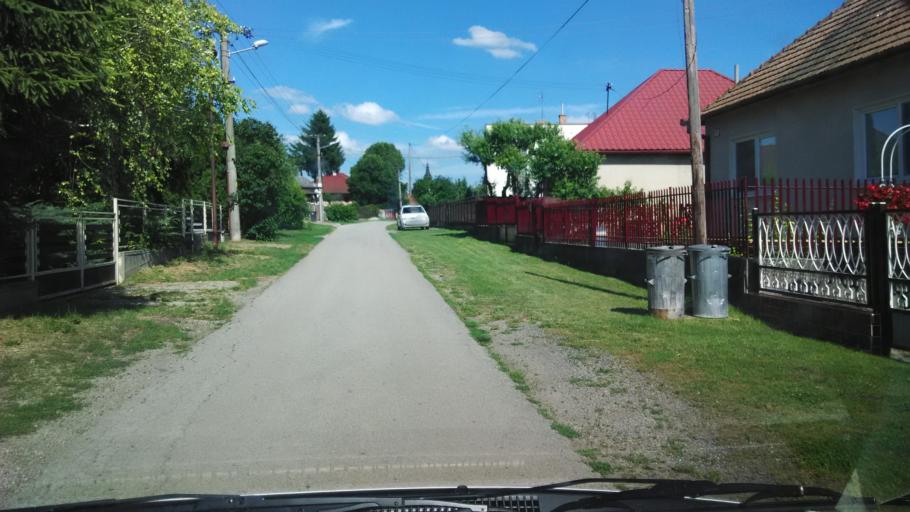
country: SK
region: Nitriansky
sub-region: Okres Nitra
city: Vrable
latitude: 48.1146
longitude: 18.3851
